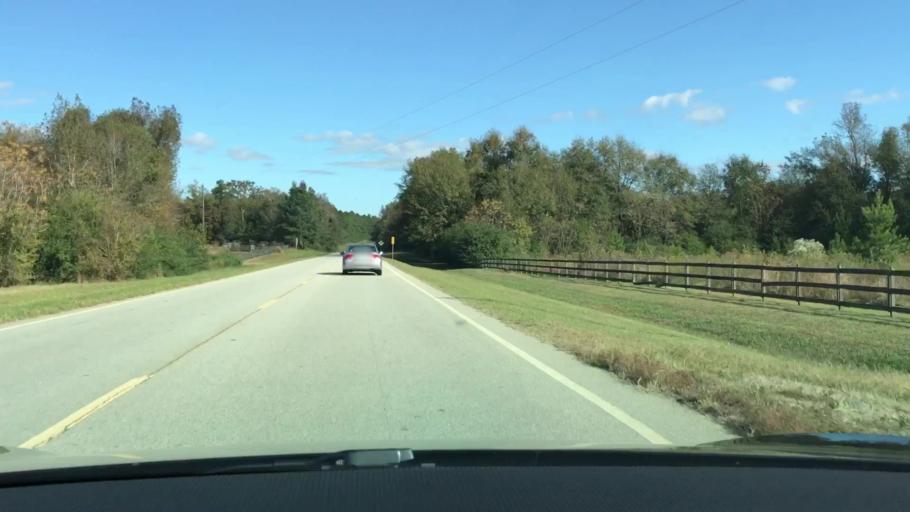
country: US
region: Georgia
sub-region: Jefferson County
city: Wrens
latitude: 33.2340
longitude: -82.4580
